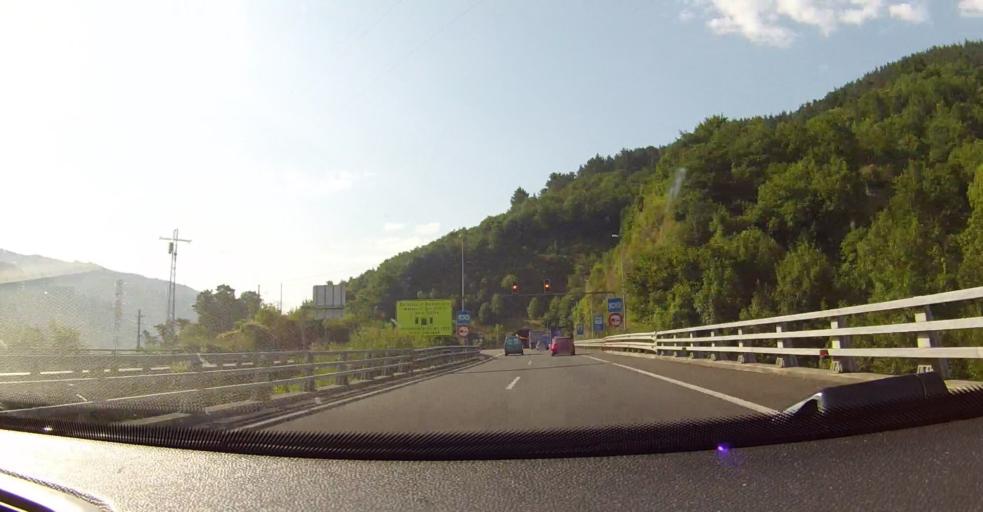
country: ES
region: Basque Country
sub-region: Provincia de Guipuzcoa
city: Elgoibar
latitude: 43.1812
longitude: -2.4277
